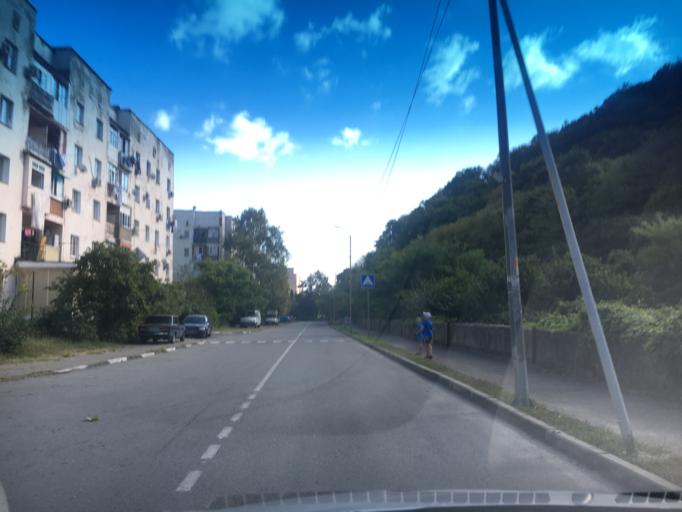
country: RU
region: Krasnodarskiy
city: Nebug
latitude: 44.1823
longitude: 38.9731
